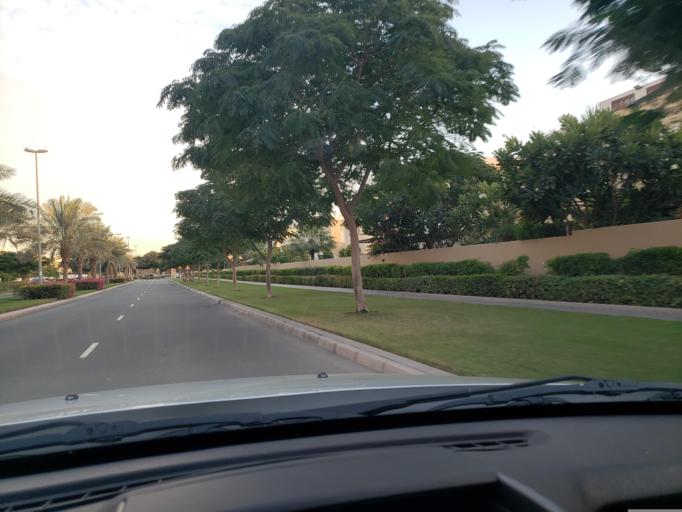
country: AE
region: Dubai
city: Dubai
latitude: 25.0260
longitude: 55.2680
